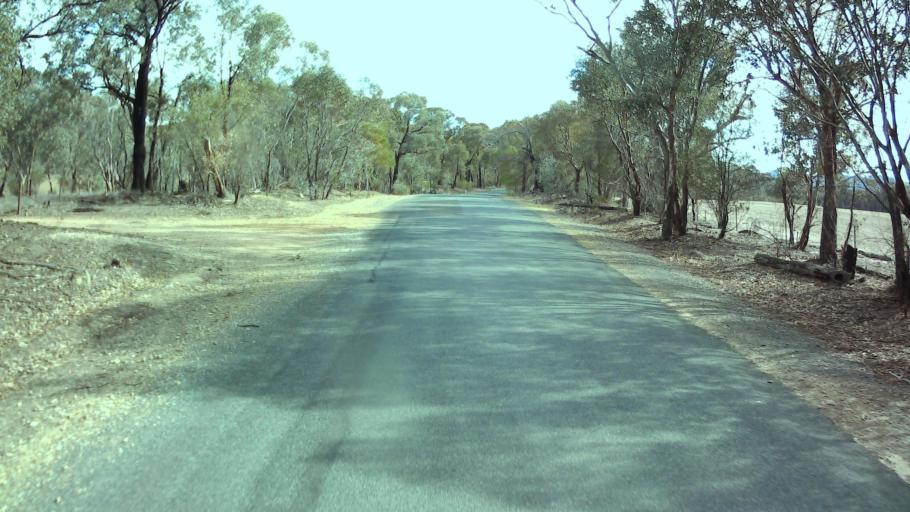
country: AU
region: New South Wales
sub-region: Weddin
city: Grenfell
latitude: -33.8735
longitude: 148.2019
